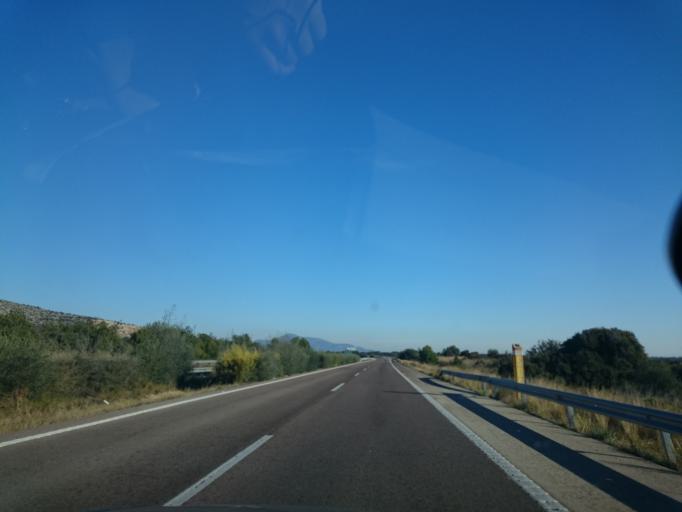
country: ES
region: Valencia
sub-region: Provincia de Castello
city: Benicarlo
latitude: 40.4645
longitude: 0.4117
